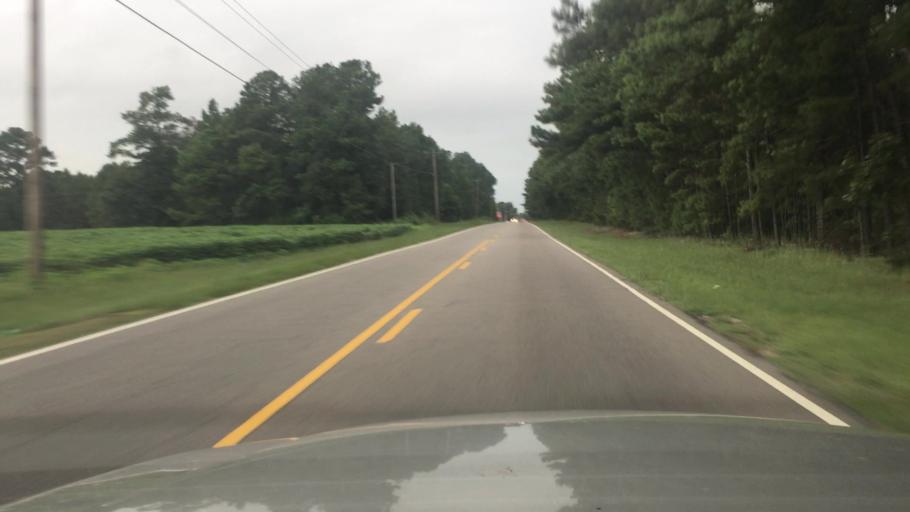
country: US
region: North Carolina
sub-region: Hoke County
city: Rockfish
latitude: 34.9743
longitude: -79.0563
